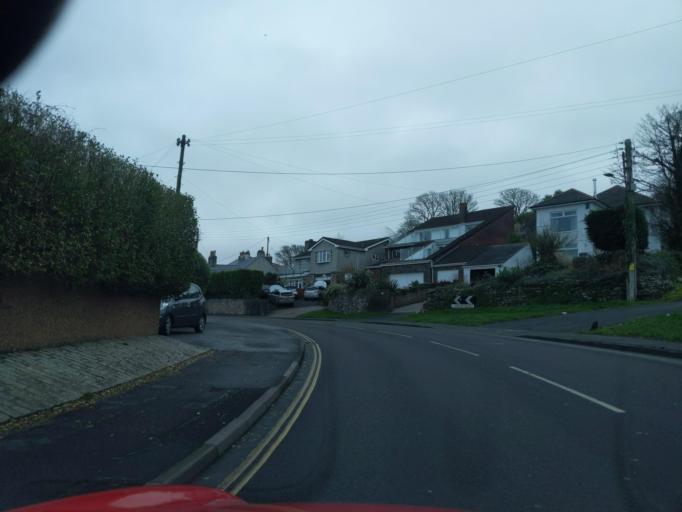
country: GB
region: England
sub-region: Plymouth
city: Plymstock
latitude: 50.3577
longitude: -4.0902
